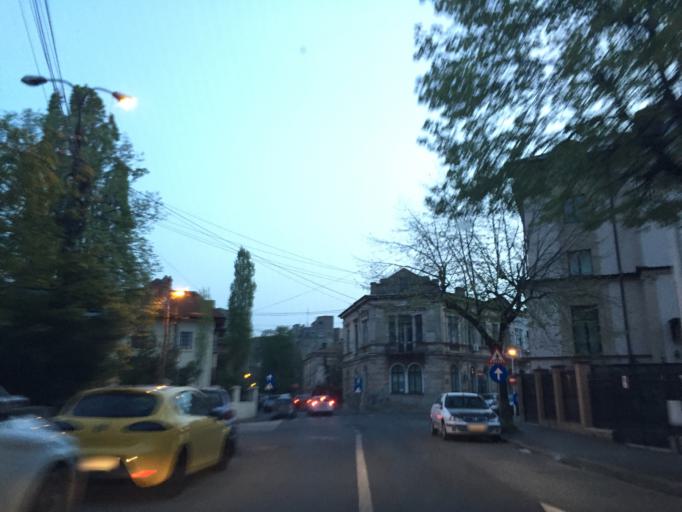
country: RO
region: Bucuresti
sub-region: Municipiul Bucuresti
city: Bucharest
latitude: 44.4357
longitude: 26.1133
